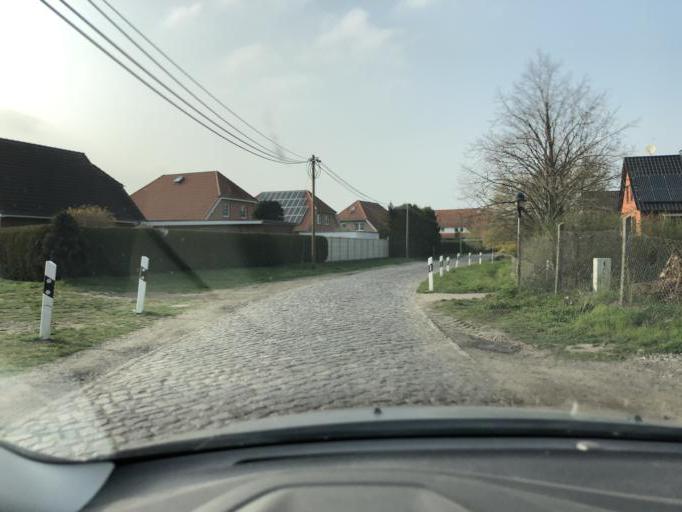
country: DE
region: Saxony-Anhalt
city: Zorbig
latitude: 51.6019
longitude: 12.1121
